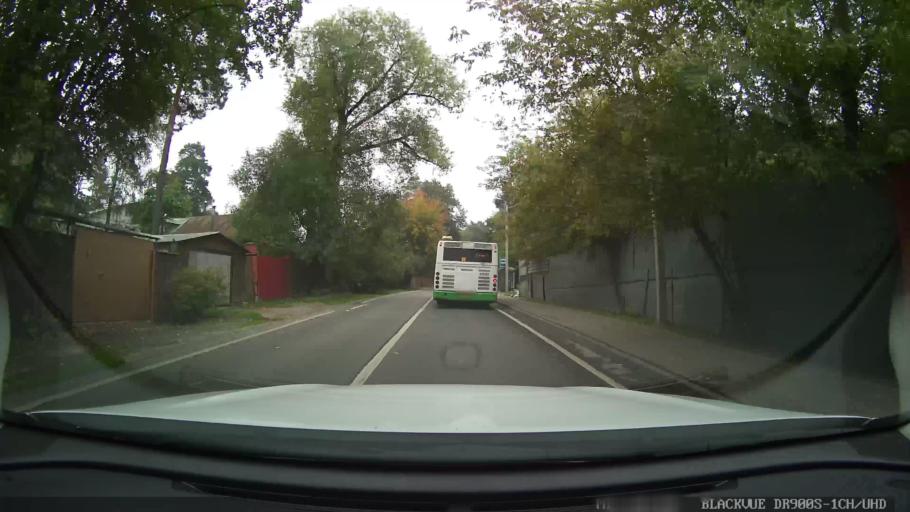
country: RU
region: Moscow
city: Novo-Peredelkino
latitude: 55.6536
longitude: 37.3551
